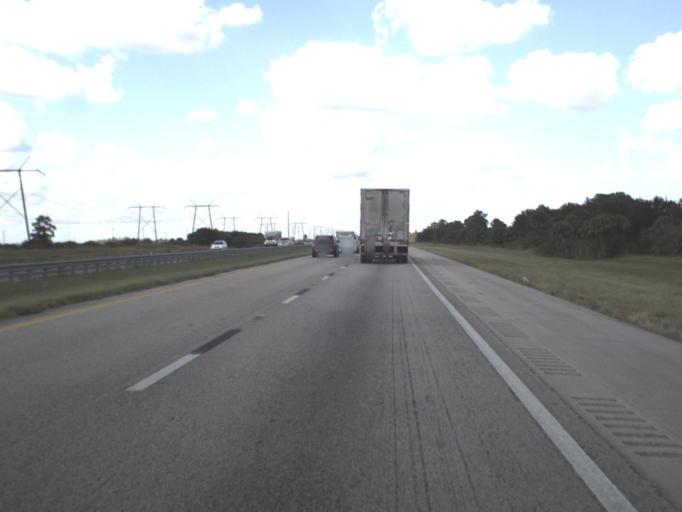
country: US
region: Florida
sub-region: Indian River County
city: West Vero Corridor
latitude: 27.4947
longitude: -80.5755
